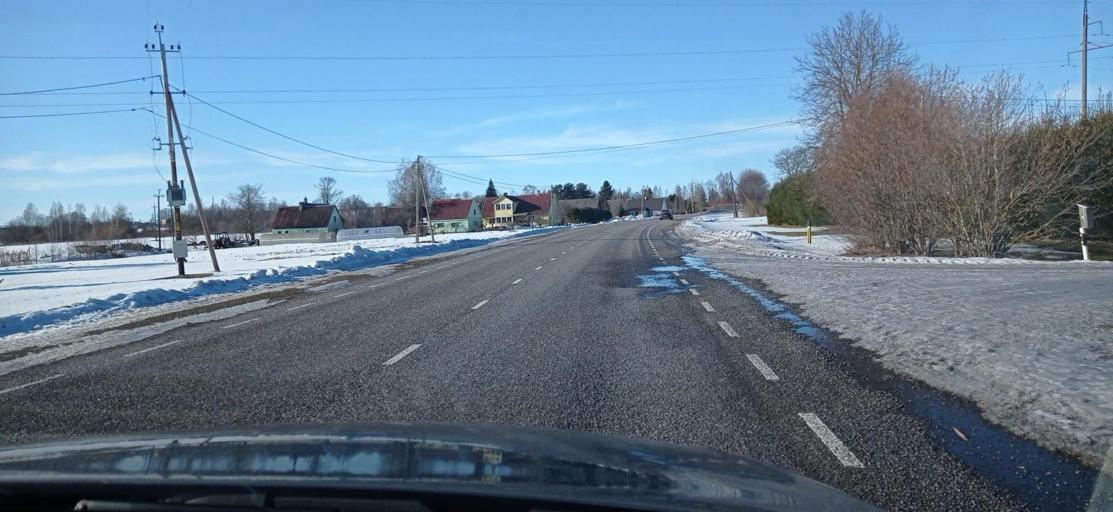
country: EE
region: Tartu
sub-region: Alatskivi vald
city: Kallaste
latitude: 58.5218
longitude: 27.0929
